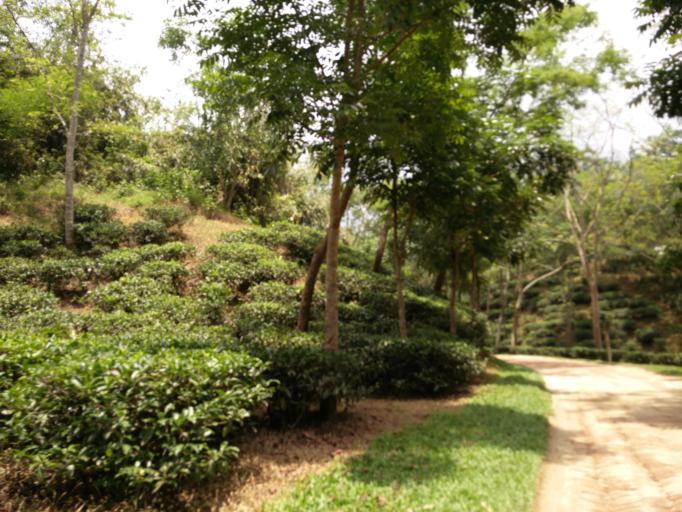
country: IN
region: Tripura
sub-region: Dhalai
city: Kamalpur
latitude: 24.3016
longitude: 91.7997
